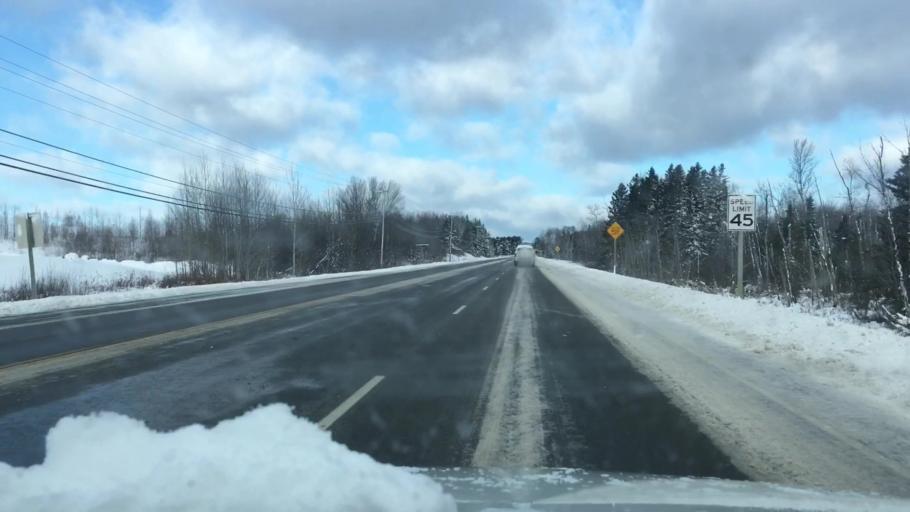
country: US
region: Maine
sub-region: Aroostook County
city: Caribou
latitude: 46.8743
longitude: -68.0041
